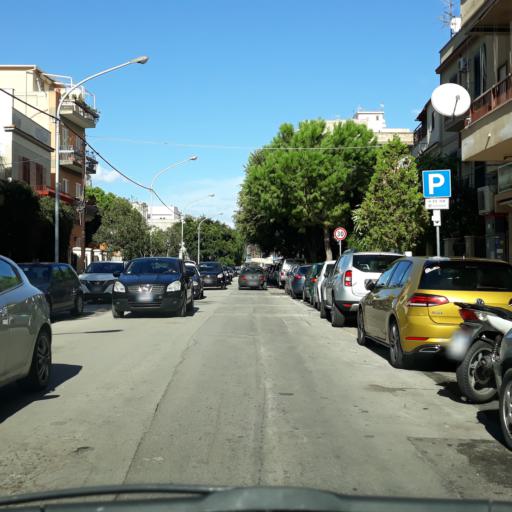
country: IT
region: Sicily
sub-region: Palermo
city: Palermo
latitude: 38.1535
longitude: 13.3706
